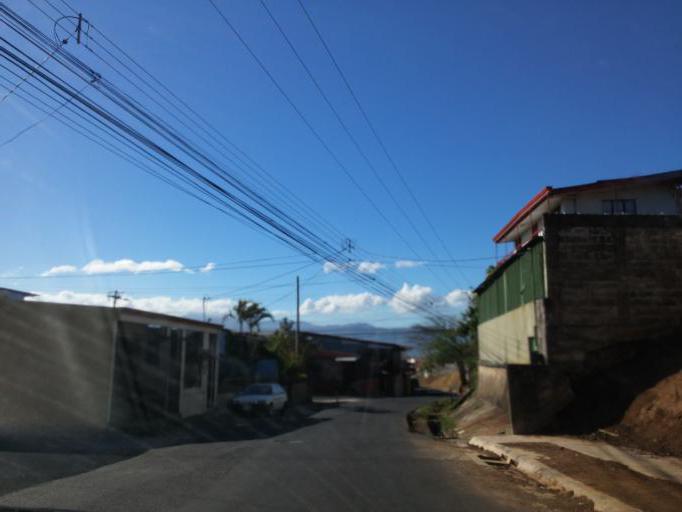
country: CR
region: Alajuela
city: Alajuela
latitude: 10.0245
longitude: -84.2013
